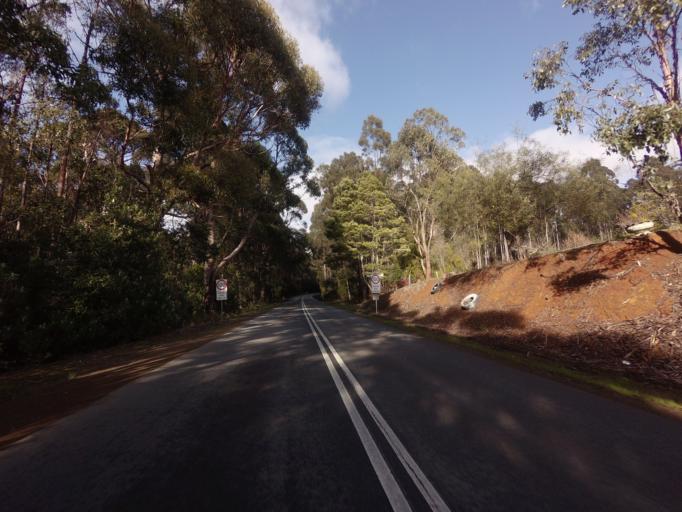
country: AU
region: Tasmania
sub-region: Huon Valley
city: Geeveston
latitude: -43.3396
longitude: 146.9711
